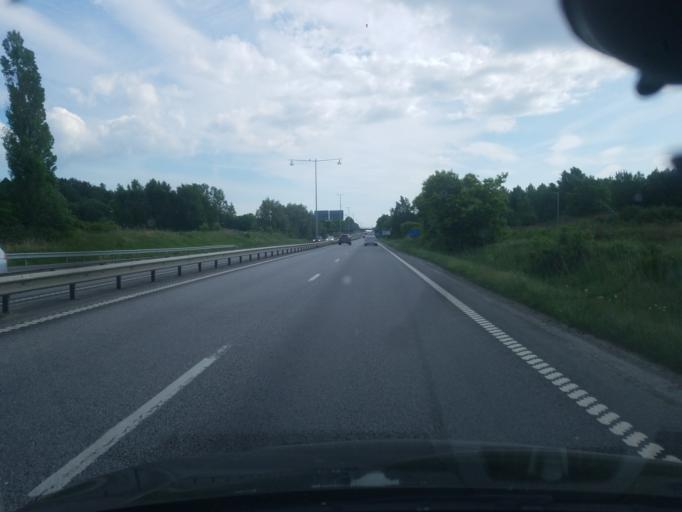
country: SE
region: Vaestra Goetaland
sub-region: Goteborg
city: Majorna
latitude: 57.6421
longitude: 11.9321
